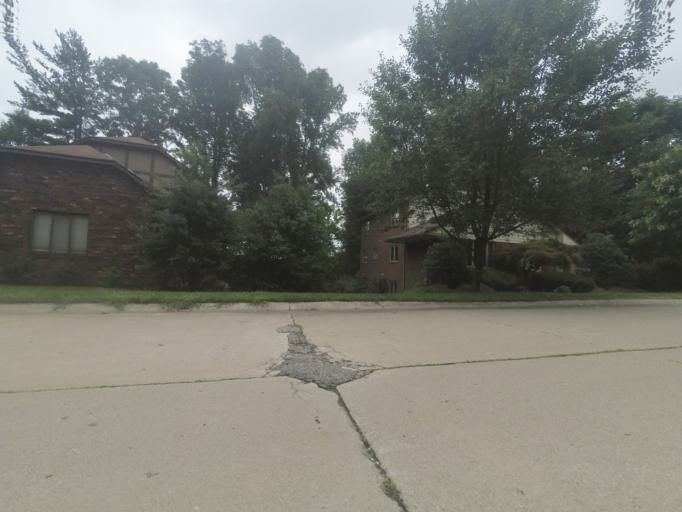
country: US
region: West Virginia
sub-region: Cabell County
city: Huntington
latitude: 38.4000
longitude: -82.3945
